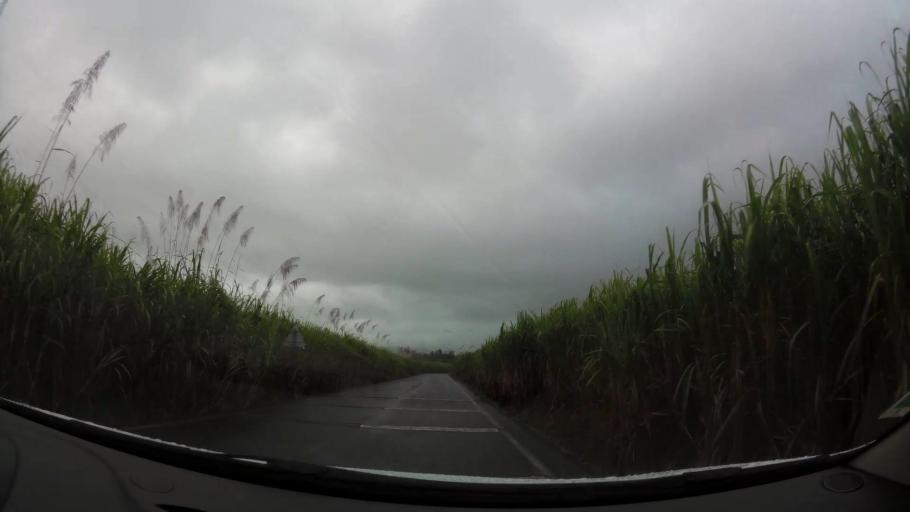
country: RE
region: Reunion
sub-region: Reunion
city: Saint-Benoit
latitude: -21.0251
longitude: 55.6917
